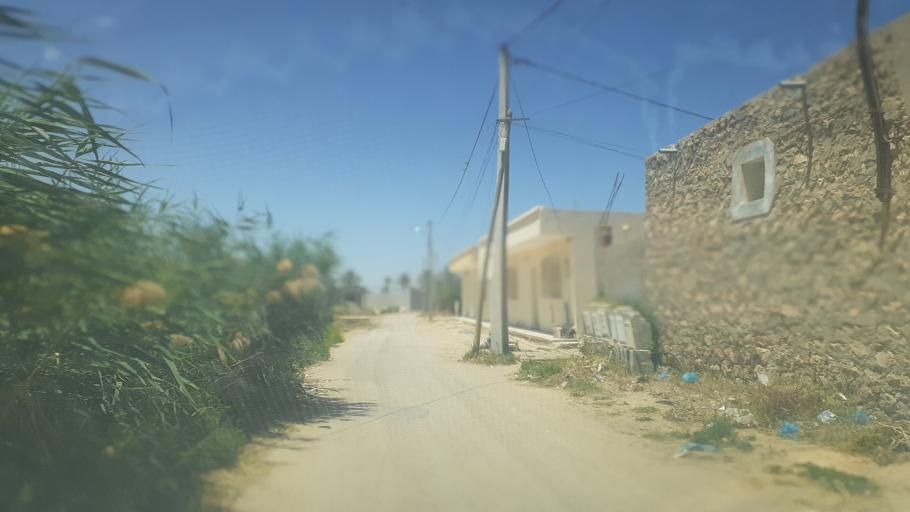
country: TN
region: Qabis
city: Gabes
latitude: 33.9308
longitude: 10.0592
